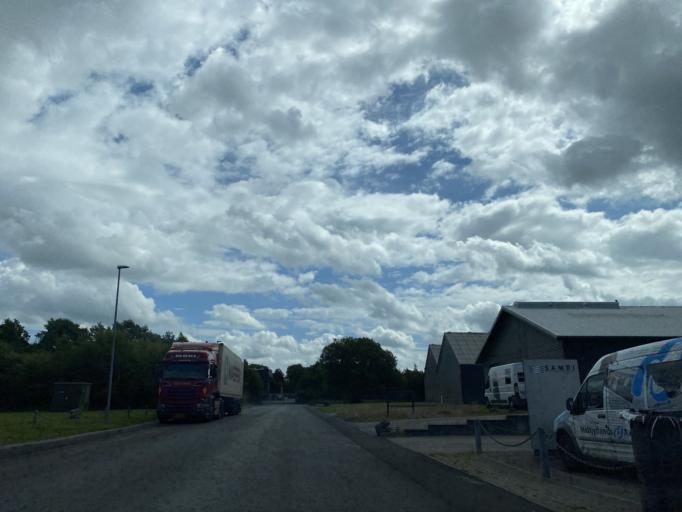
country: DK
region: Central Jutland
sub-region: Silkeborg Kommune
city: Silkeborg
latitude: 56.2066
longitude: 9.5771
